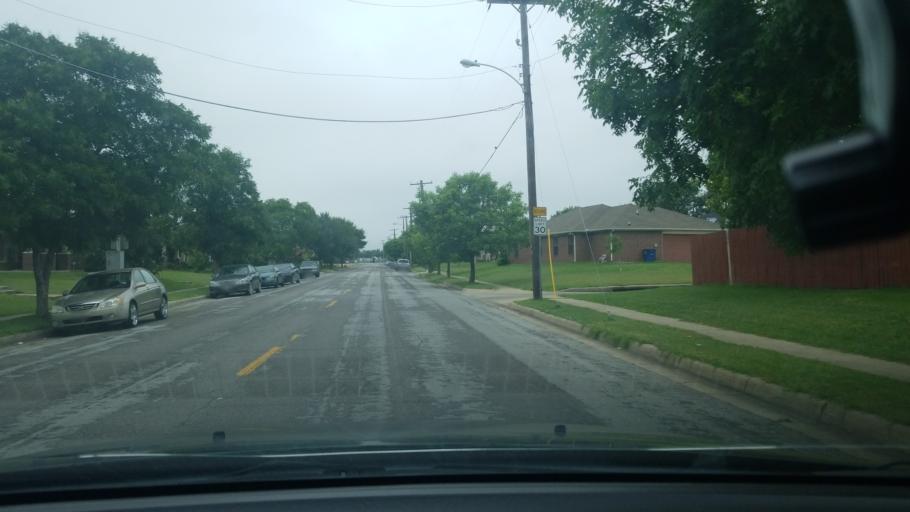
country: US
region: Texas
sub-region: Dallas County
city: Balch Springs
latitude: 32.7546
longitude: -96.6873
